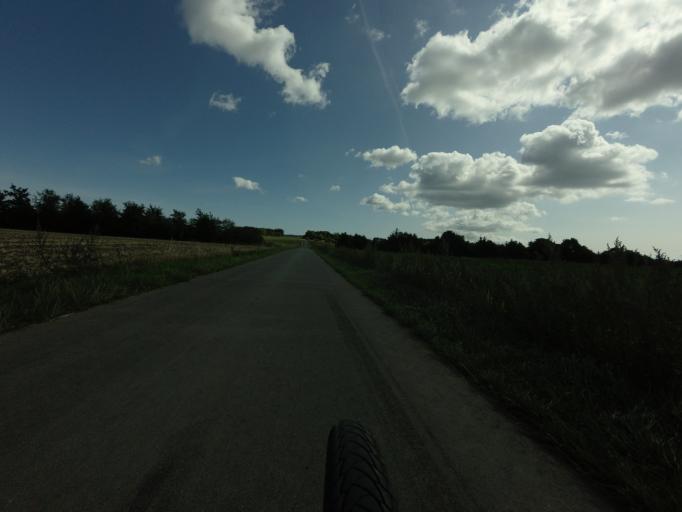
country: DK
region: Zealand
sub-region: Vordingborg Kommune
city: Stege
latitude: 54.9725
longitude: 12.4346
